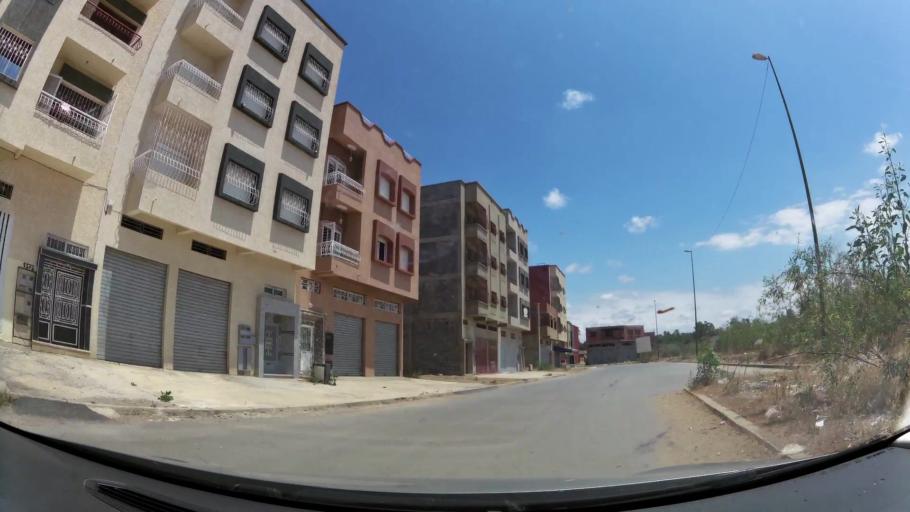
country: MA
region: Gharb-Chrarda-Beni Hssen
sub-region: Kenitra Province
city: Kenitra
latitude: 34.2302
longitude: -6.6084
